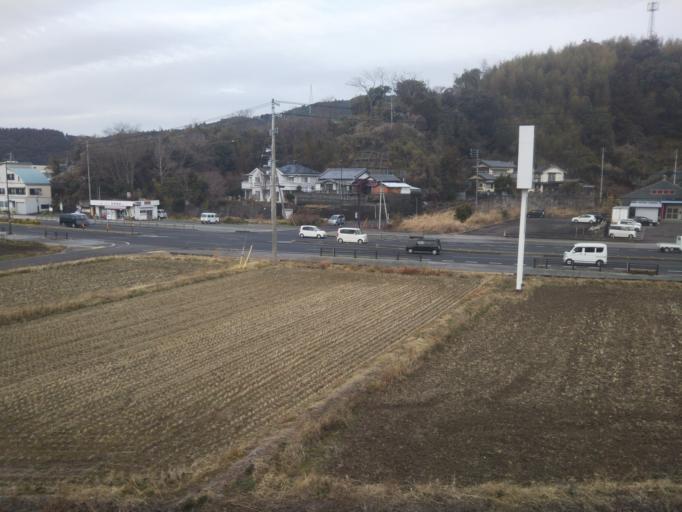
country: JP
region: Kochi
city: Nakamura
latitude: 32.9854
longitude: 132.9617
